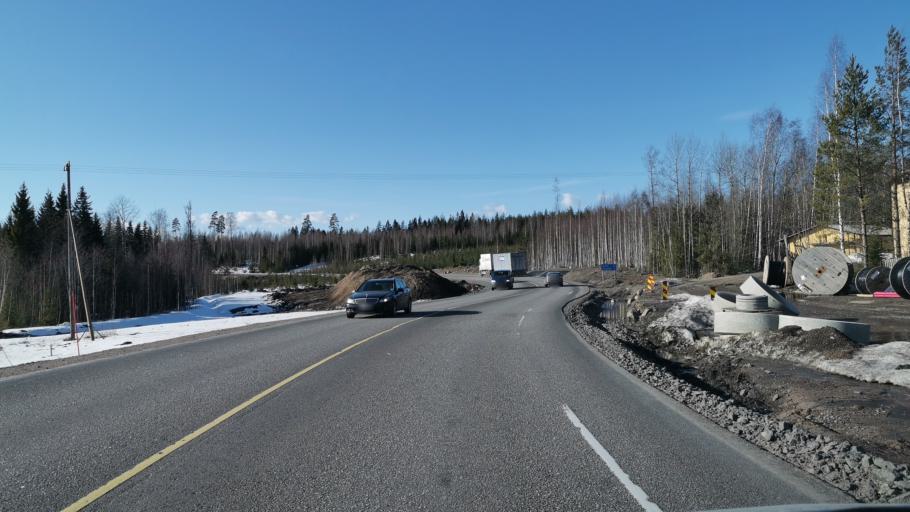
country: FI
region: Kymenlaakso
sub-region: Kouvola
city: Kouvola
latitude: 60.8679
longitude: 26.5522
